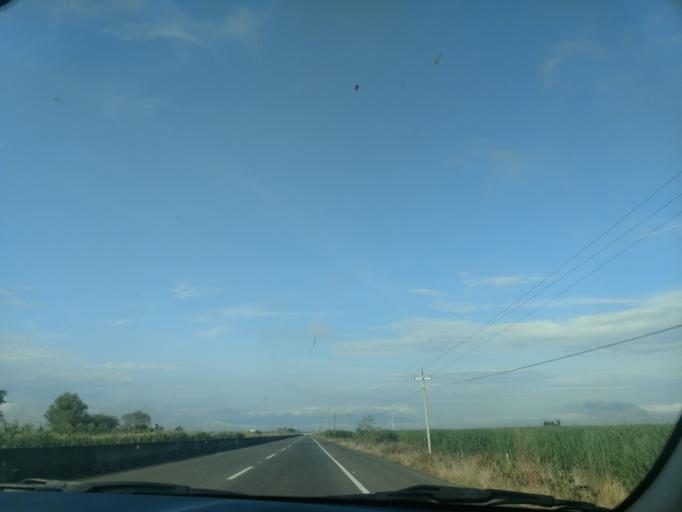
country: MX
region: Jalisco
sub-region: San Martin Hidalgo
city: Trapiche de Abra
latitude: 20.5606
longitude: -103.8764
